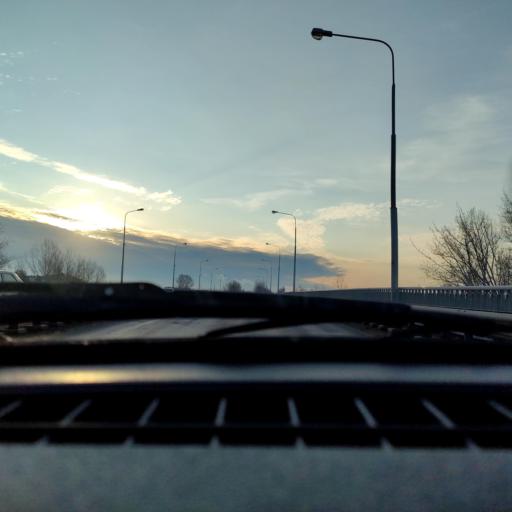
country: RU
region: Bashkortostan
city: Iglino
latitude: 54.7884
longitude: 56.2166
